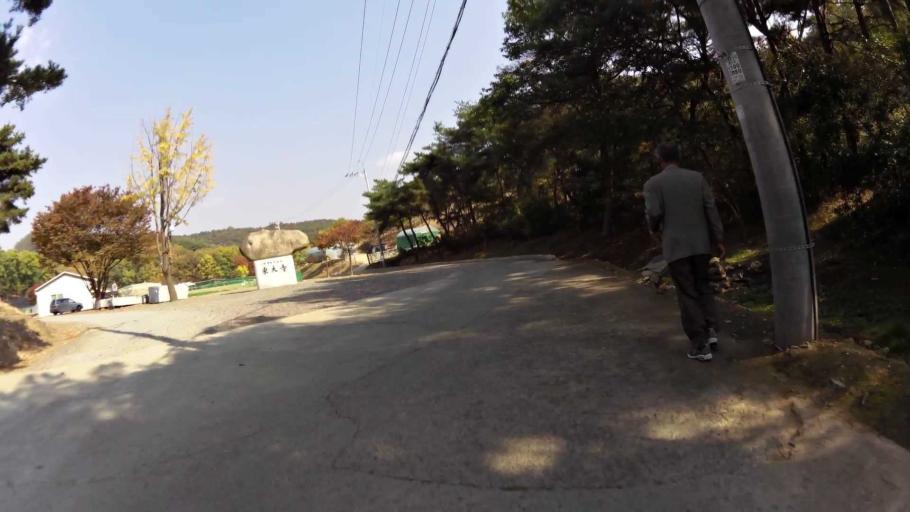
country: KR
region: Daegu
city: Daegu
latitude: 35.8584
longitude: 128.6608
